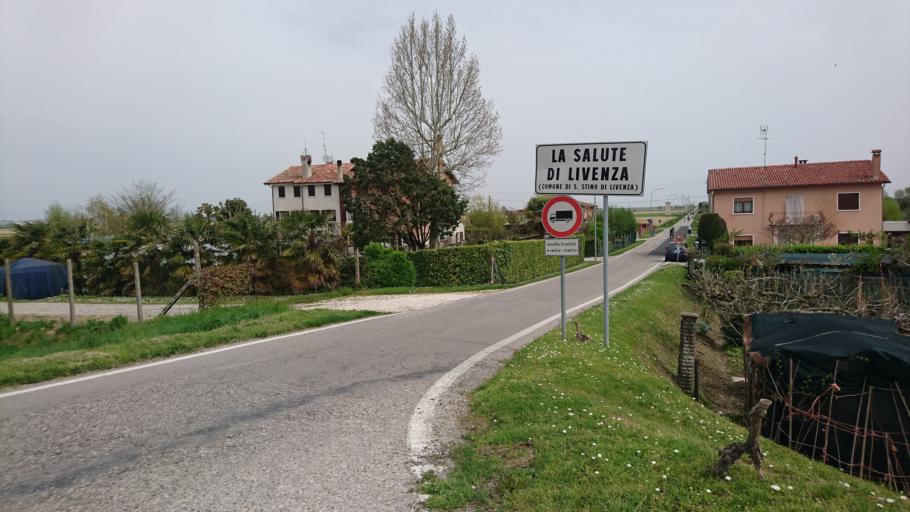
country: IT
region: Veneto
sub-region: Provincia di Venezia
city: La Salute di Livenza
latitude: 45.6466
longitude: 12.8209
